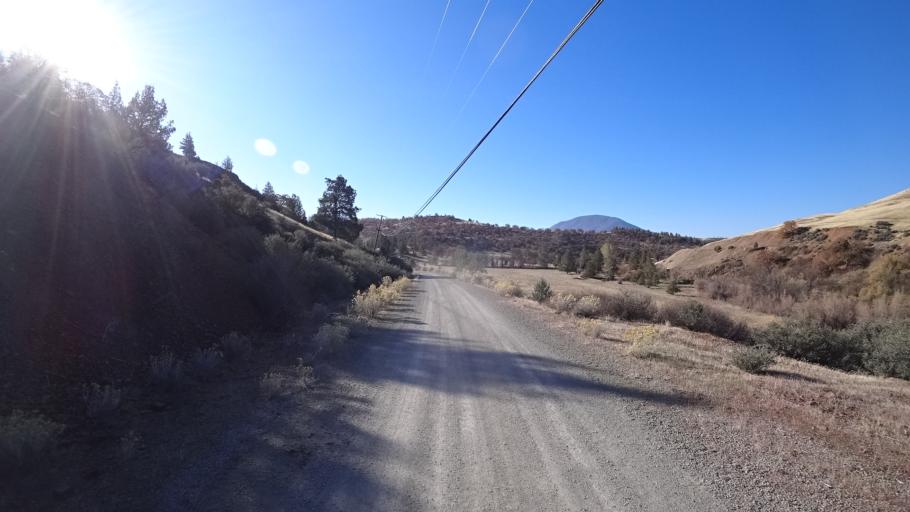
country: US
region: California
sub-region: Siskiyou County
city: Montague
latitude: 41.9206
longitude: -122.4484
